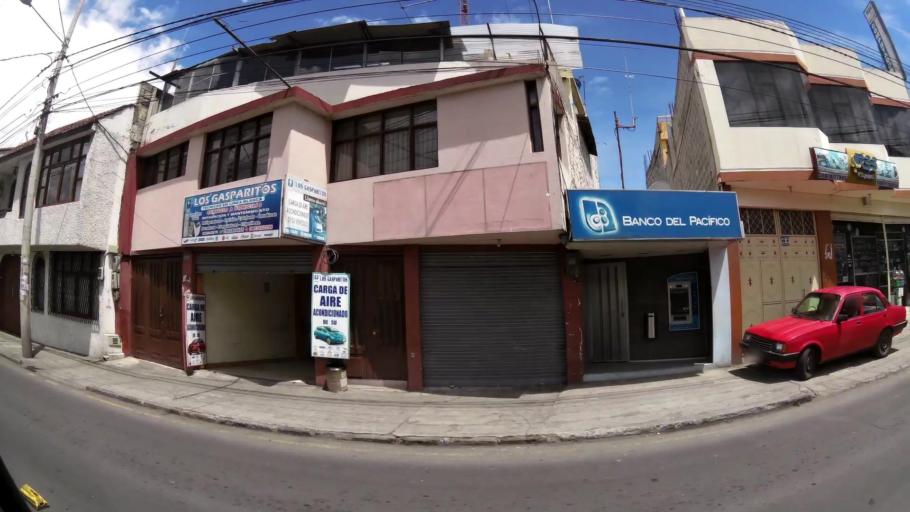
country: EC
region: Tungurahua
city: Ambato
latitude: -1.2515
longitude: -78.6327
